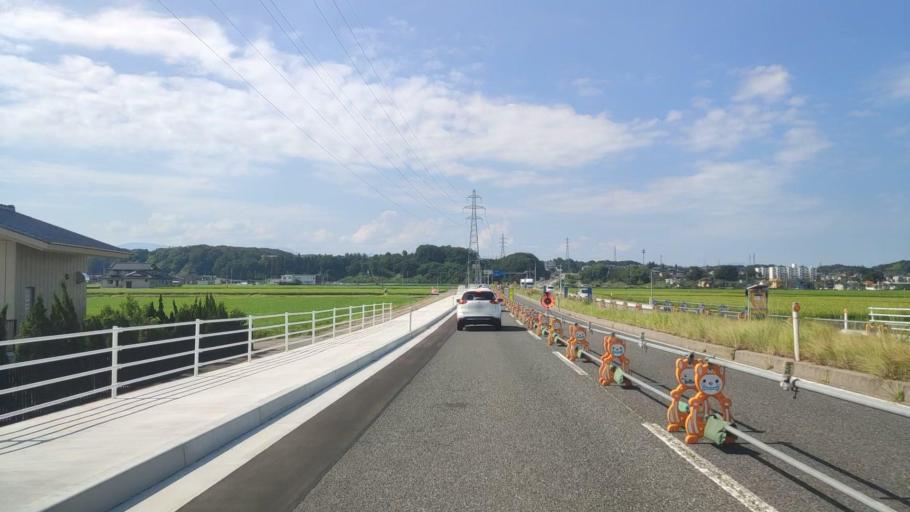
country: JP
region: Ishikawa
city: Komatsu
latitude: 36.4048
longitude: 136.5077
